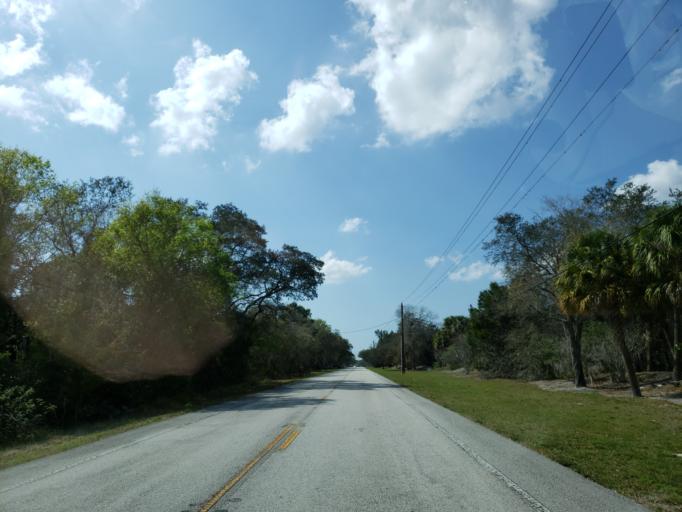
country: US
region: Florida
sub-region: Hillsborough County
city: Keystone
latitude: 28.1451
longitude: -82.6003
